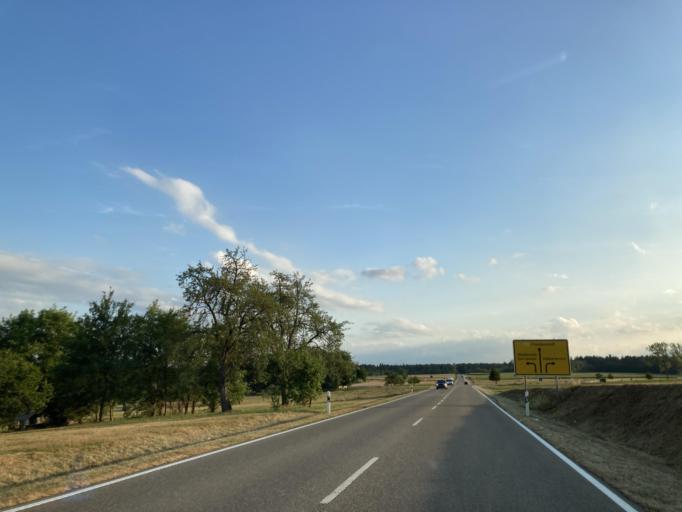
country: DE
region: Baden-Wuerttemberg
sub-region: Karlsruhe Region
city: Pfalzgrafenweiler
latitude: 48.5240
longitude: 8.5460
